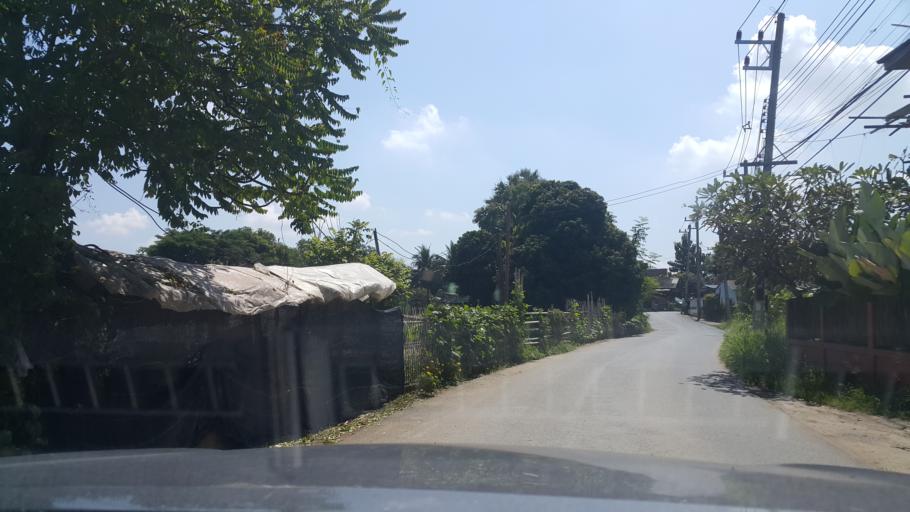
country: TH
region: Chiang Mai
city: Chiang Mai
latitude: 18.8469
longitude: 98.9840
